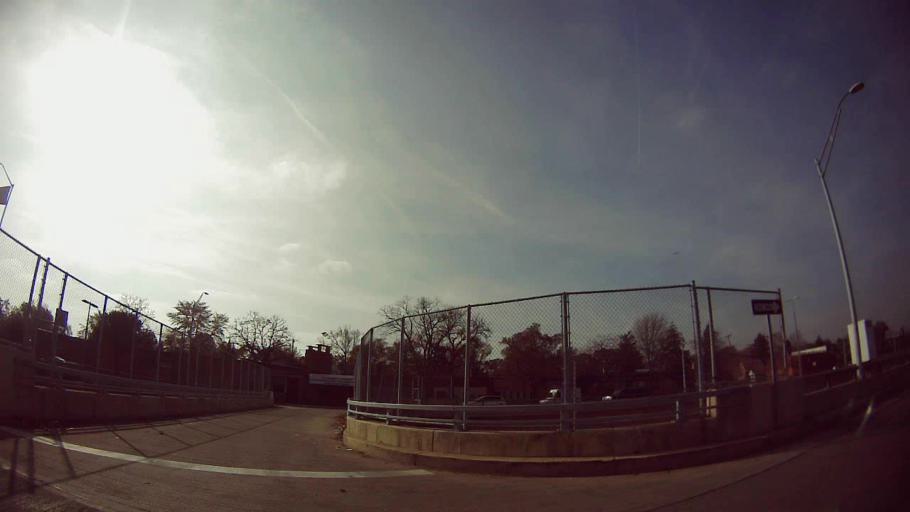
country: US
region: Michigan
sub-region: Oakland County
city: Oak Park
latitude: 42.4254
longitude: -83.1803
